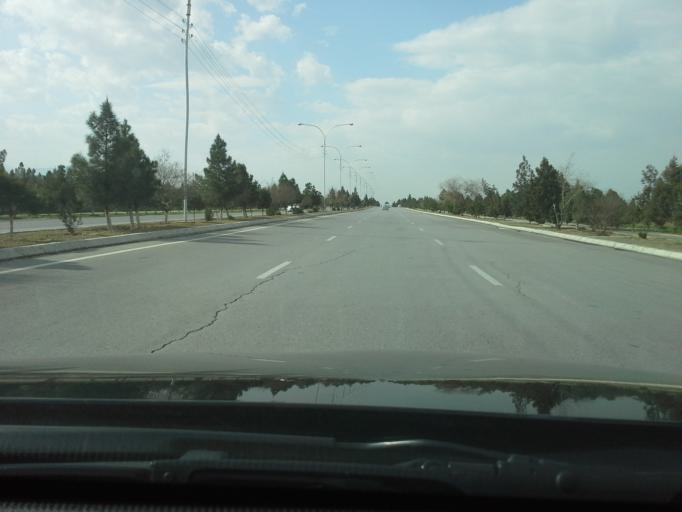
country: TM
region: Ahal
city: Ashgabat
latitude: 37.9666
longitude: 58.3043
